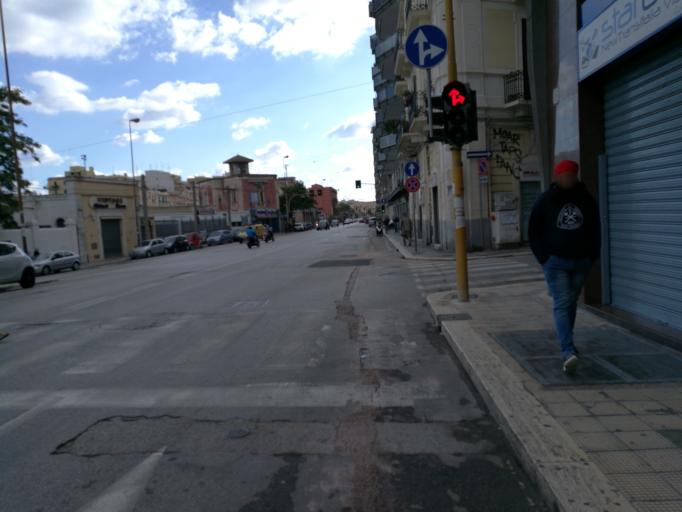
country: IT
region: Apulia
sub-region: Provincia di Bari
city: Bari
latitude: 41.1173
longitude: 16.8750
